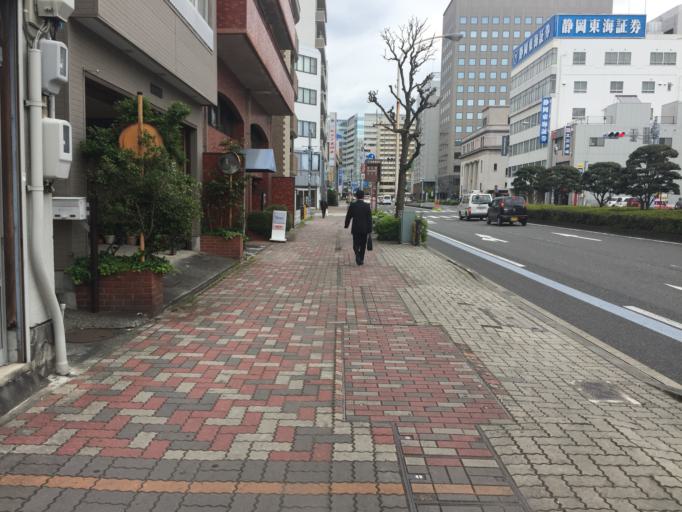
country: JP
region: Shizuoka
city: Shizuoka-shi
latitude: 34.9750
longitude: 138.3779
